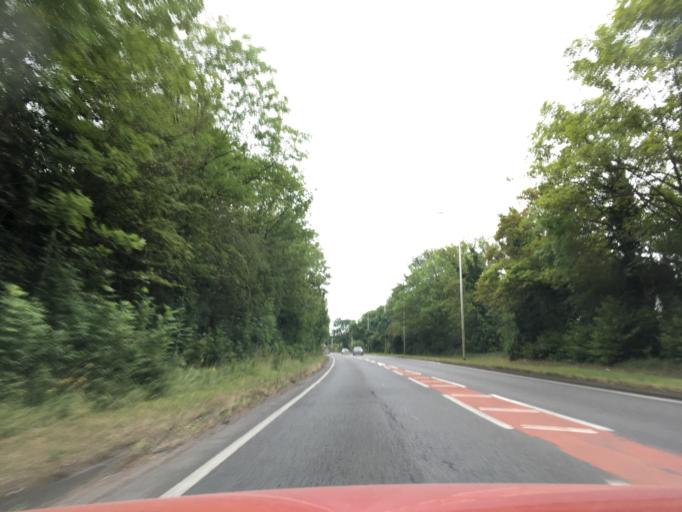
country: GB
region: England
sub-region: Hertfordshire
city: Markyate
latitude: 51.8313
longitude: -0.4499
